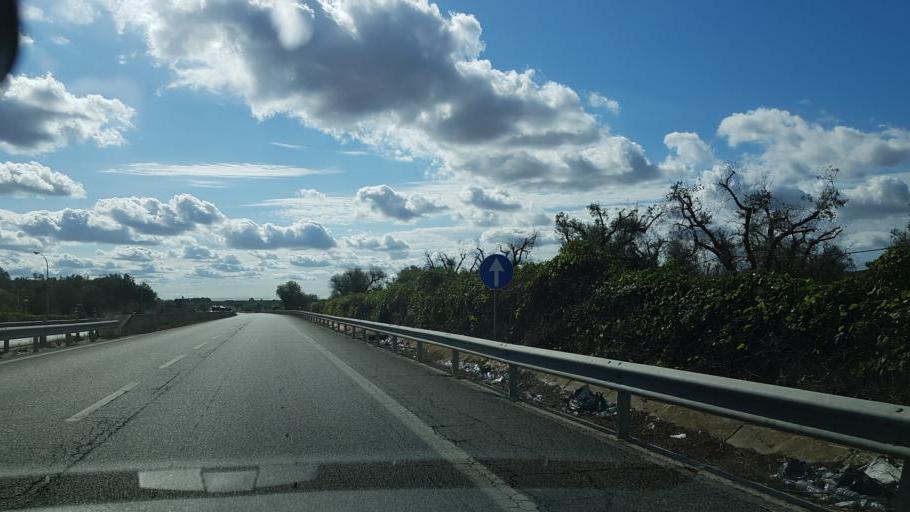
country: IT
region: Apulia
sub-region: Provincia di Brindisi
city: Torchiarolo
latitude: 40.4913
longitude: 18.0378
